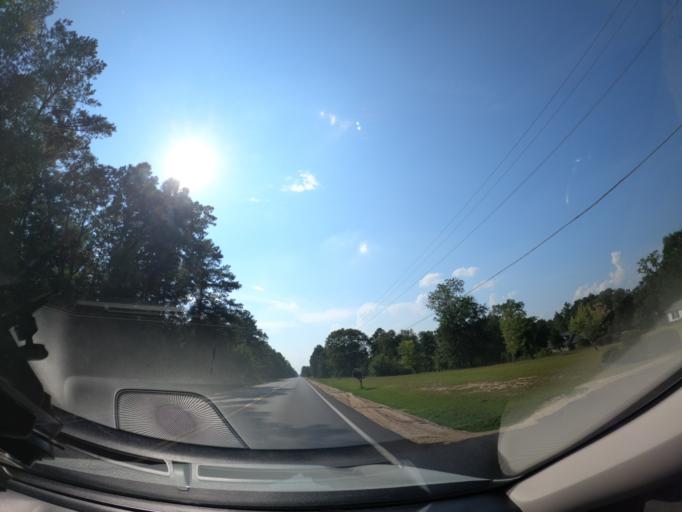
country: US
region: South Carolina
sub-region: Aiken County
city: New Ellenton
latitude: 33.4005
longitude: -81.7614
